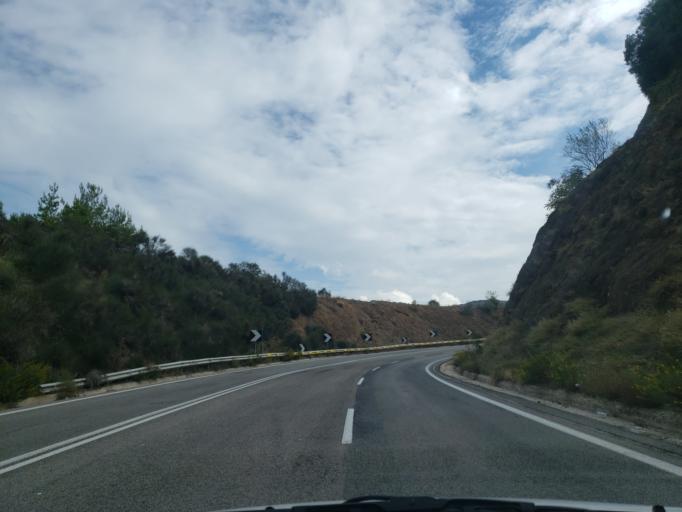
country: GR
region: Central Greece
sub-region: Nomos Fthiotidos
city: Stavros
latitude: 38.9992
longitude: 22.3701
